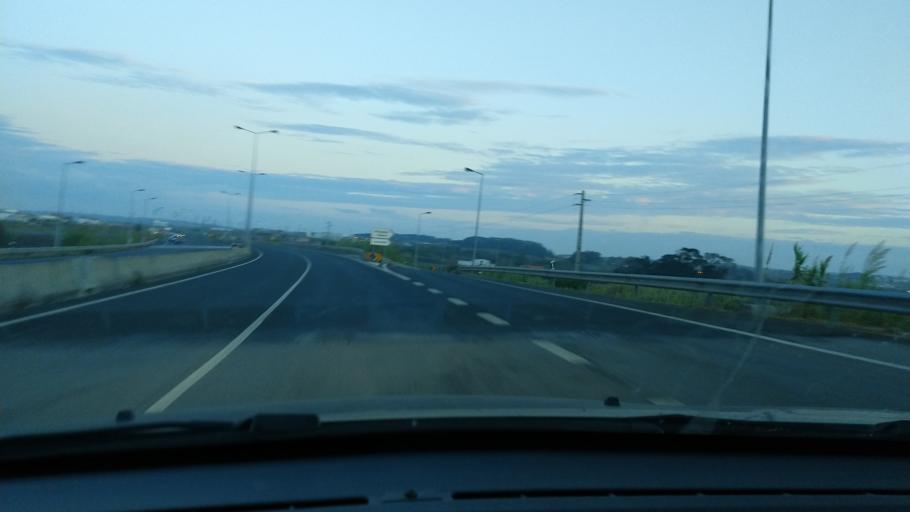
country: PT
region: Leiria
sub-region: Peniche
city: Atouguia da Baleia
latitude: 39.3315
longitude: -9.3326
